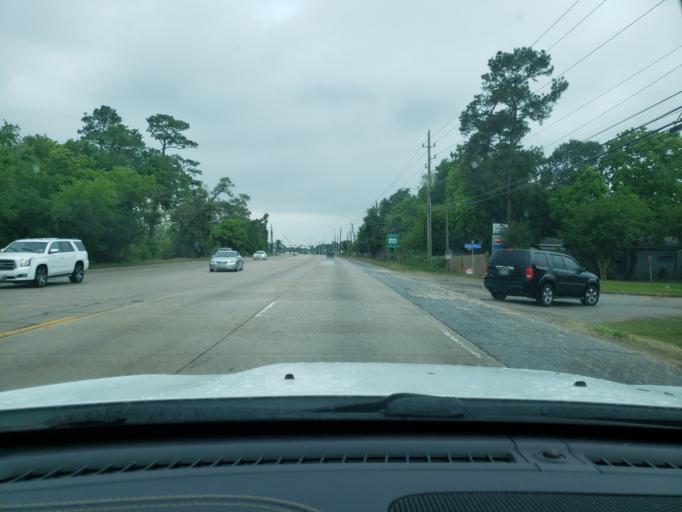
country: US
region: Texas
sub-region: Chambers County
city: Mont Belvieu
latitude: 29.7819
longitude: -94.9128
